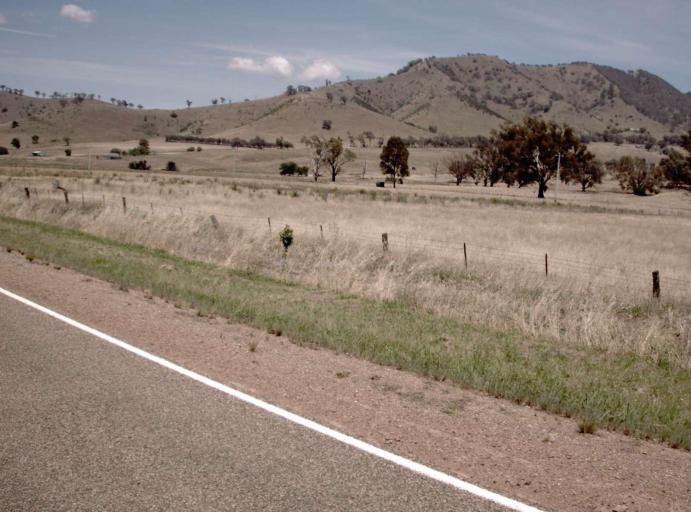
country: AU
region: Victoria
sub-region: East Gippsland
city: Bairnsdale
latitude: -37.2376
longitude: 147.7140
